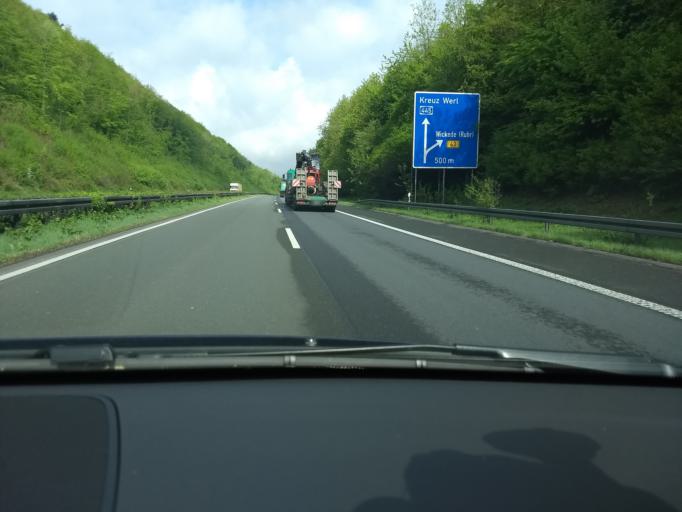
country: DE
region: North Rhine-Westphalia
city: Wickede
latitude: 51.5112
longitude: 7.9072
